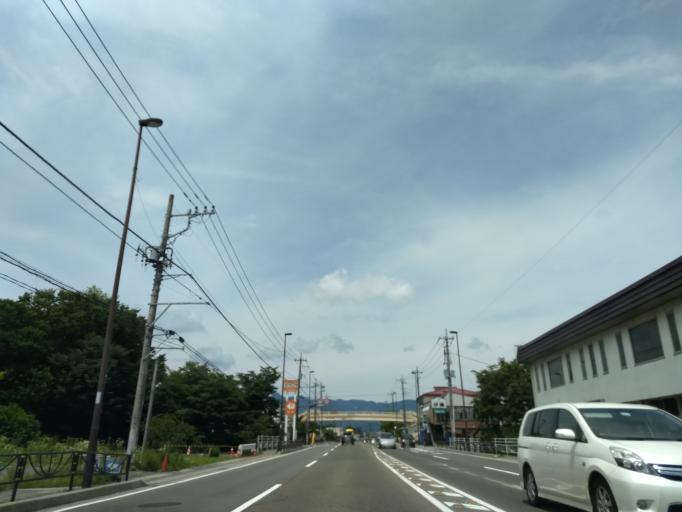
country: JP
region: Yamanashi
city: Fujikawaguchiko
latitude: 35.4761
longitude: 138.7900
